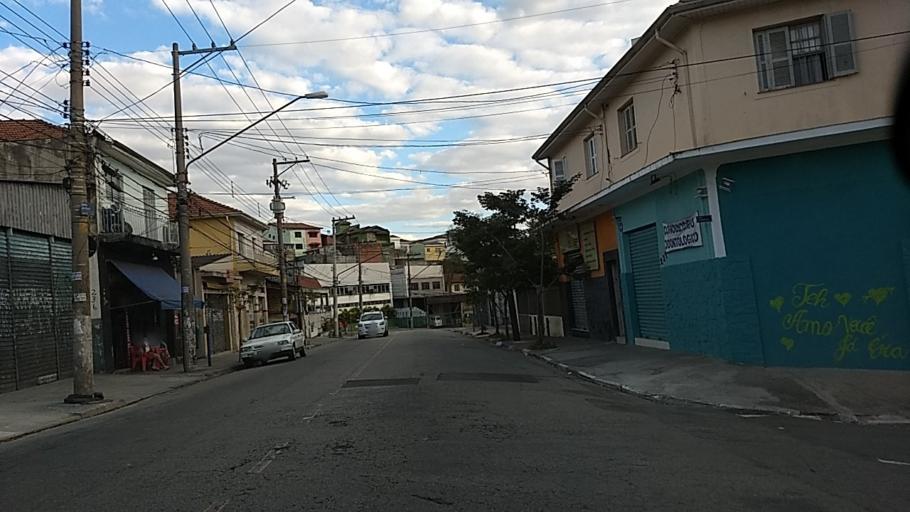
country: BR
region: Sao Paulo
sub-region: Sao Paulo
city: Sao Paulo
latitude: -23.4962
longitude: -46.5982
